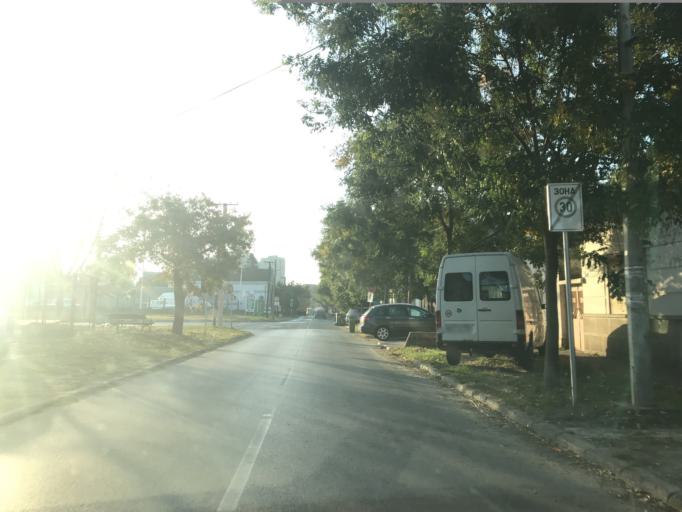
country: RS
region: Autonomna Pokrajina Vojvodina
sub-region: Juznobacki Okrug
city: Novi Sad
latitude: 45.2654
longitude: 19.8499
